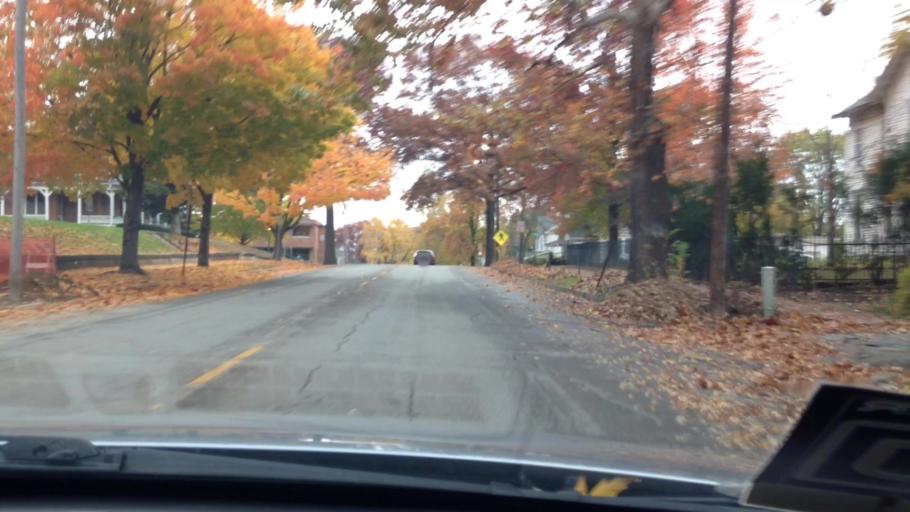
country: US
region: Kansas
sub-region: Leavenworth County
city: Leavenworth
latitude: 39.3057
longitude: -94.9175
